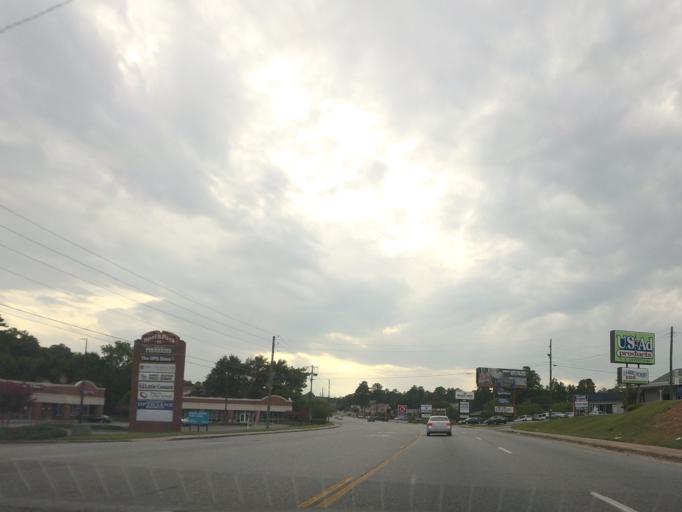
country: US
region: Georgia
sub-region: Bibb County
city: Macon
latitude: 32.8973
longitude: -83.6919
